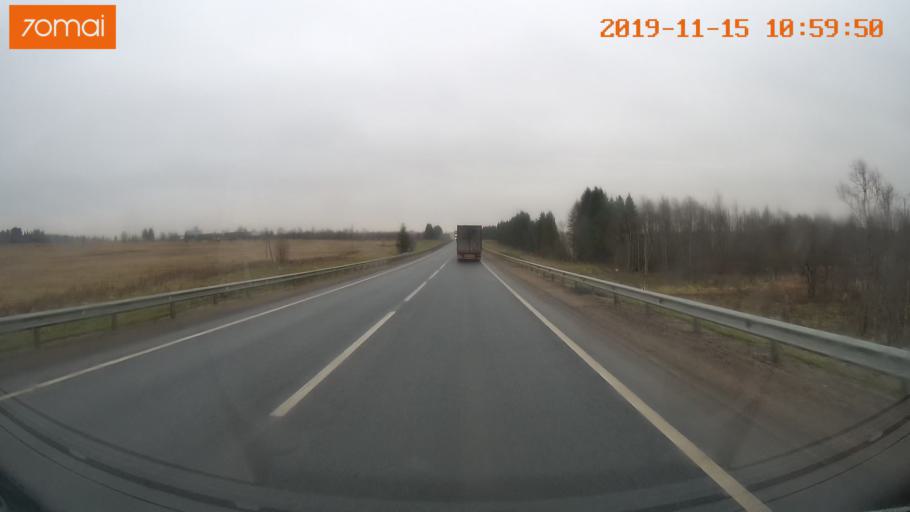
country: RU
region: Vologda
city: Chebsara
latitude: 59.1399
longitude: 38.8861
